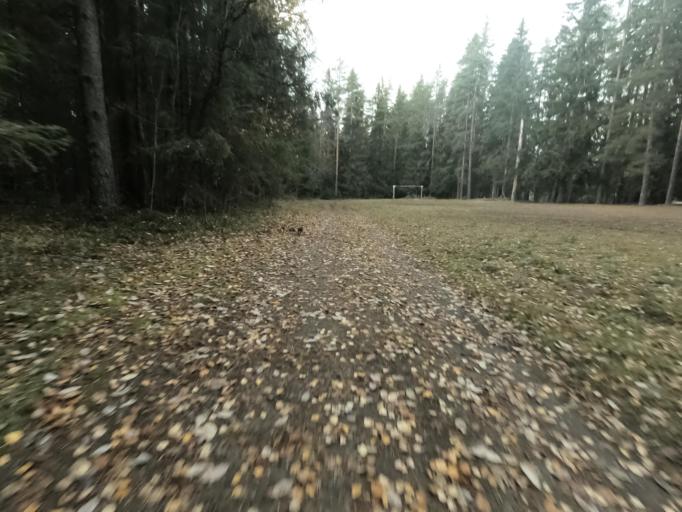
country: RU
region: Leningrad
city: Leninskoye
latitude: 60.1964
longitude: 29.8482
